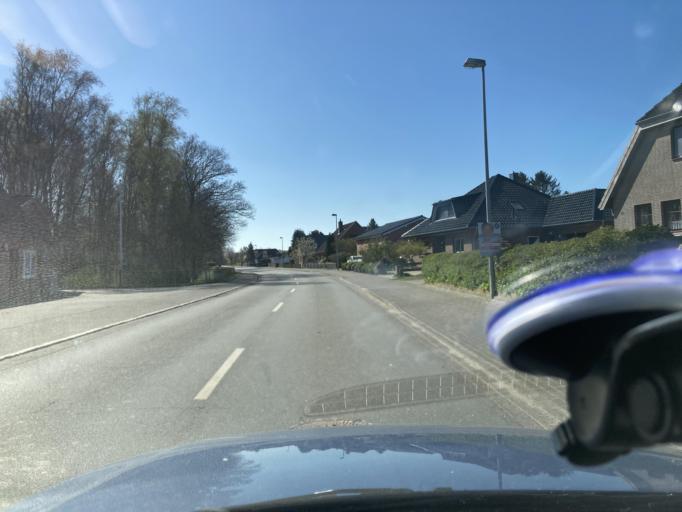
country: DE
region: Schleswig-Holstein
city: Sarzbuttel
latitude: 54.1158
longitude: 9.1851
